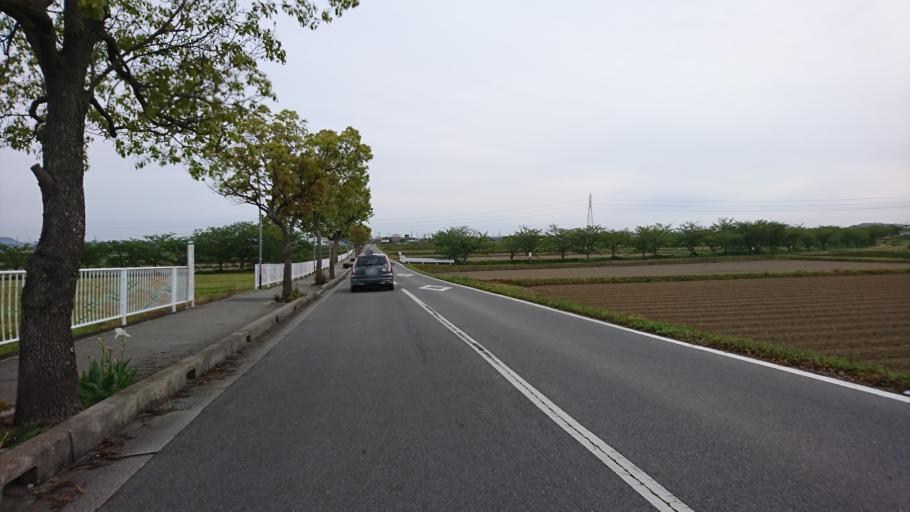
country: JP
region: Hyogo
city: Kakogawacho-honmachi
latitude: 34.7538
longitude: 134.9072
